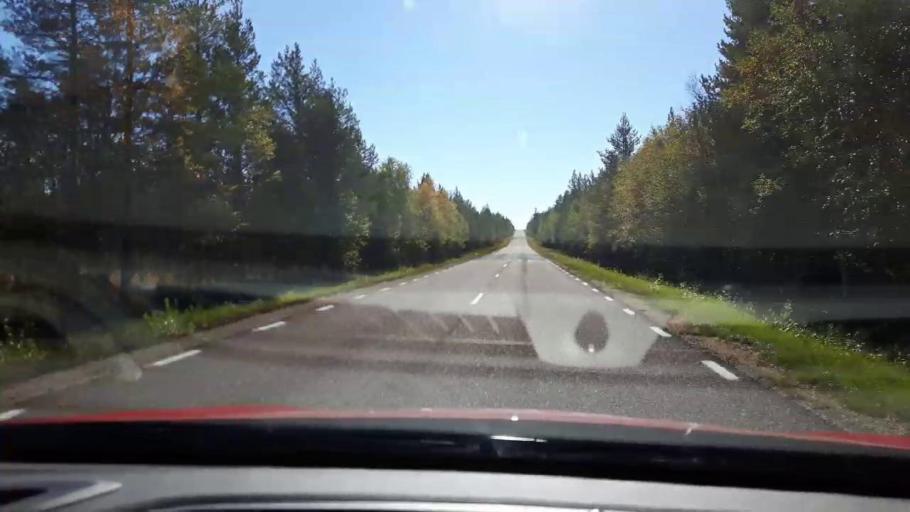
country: SE
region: Jaemtland
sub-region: Harjedalens Kommun
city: Sveg
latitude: 61.7374
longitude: 14.1630
